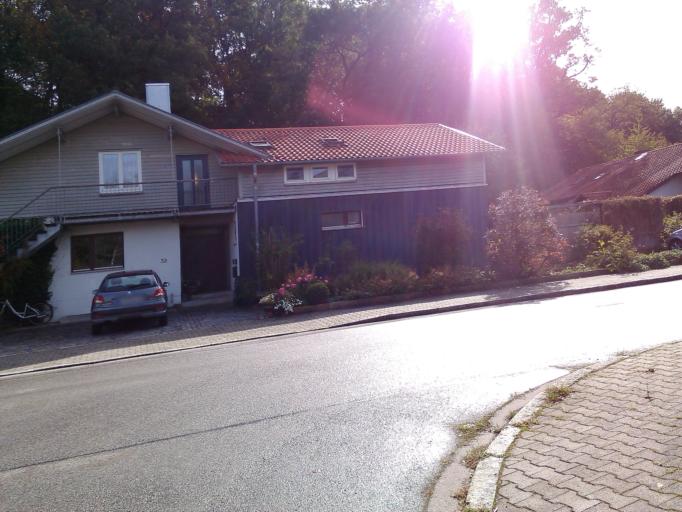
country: DE
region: Bavaria
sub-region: Upper Bavaria
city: Gauting
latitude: 48.0681
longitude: 11.3894
